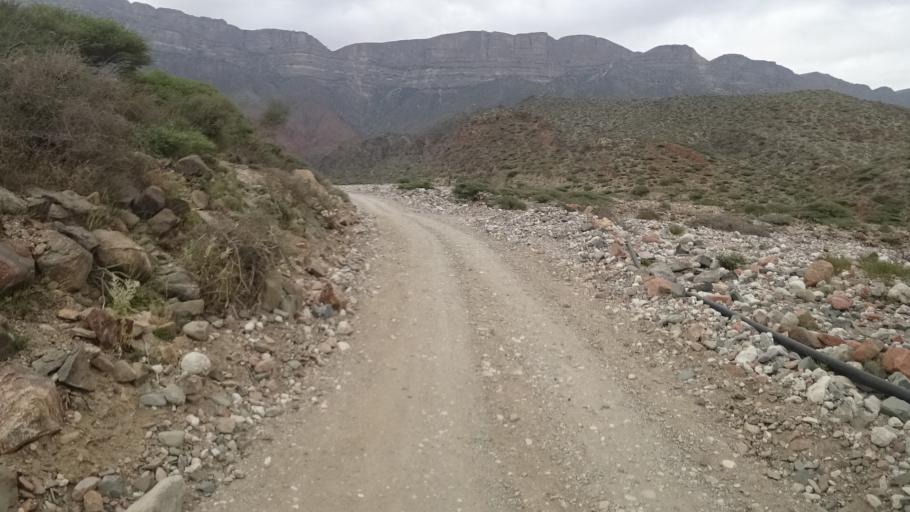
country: OM
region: Zufar
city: Salalah
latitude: 17.1763
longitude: 54.9501
